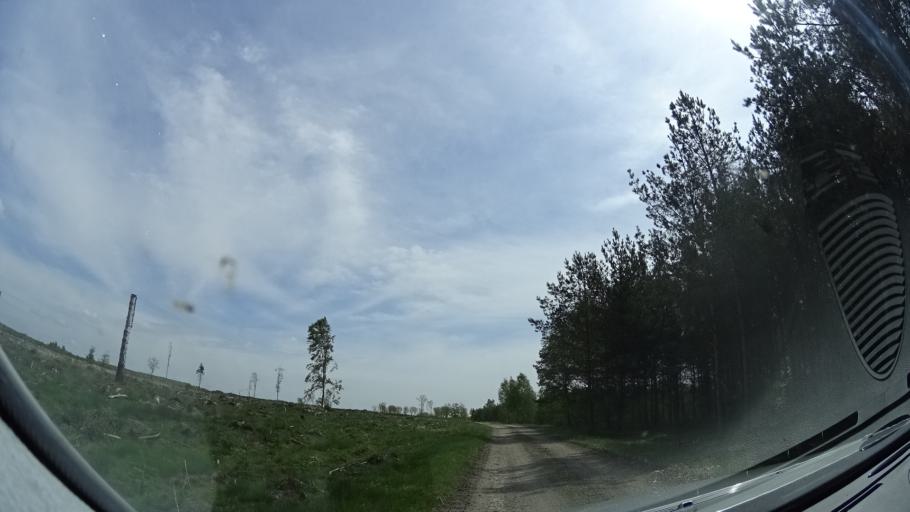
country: SE
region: Skane
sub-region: Sjobo Kommun
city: Sjoebo
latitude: 55.6667
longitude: 13.6528
